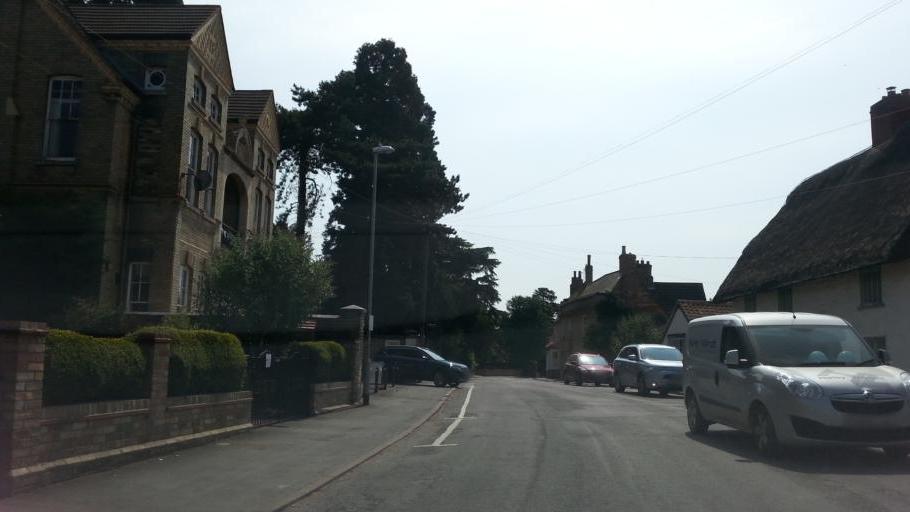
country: GB
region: England
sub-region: Cambridgeshire
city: Brampton
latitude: 52.3218
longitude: -0.2239
